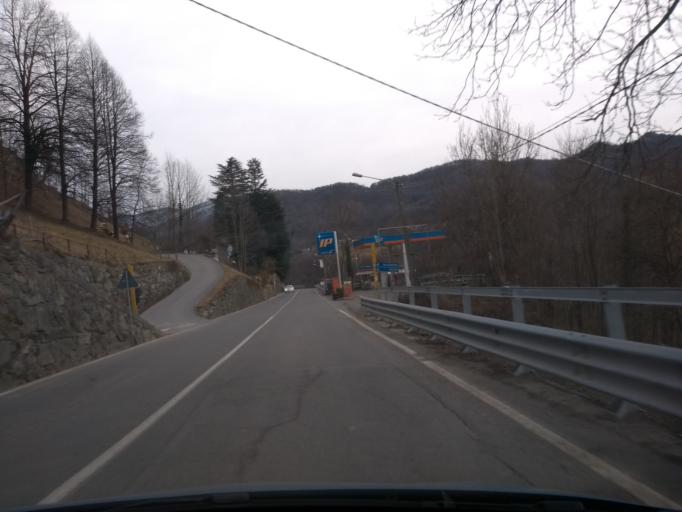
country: IT
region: Piedmont
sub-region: Provincia di Torino
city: Viu
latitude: 45.2393
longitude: 7.3807
